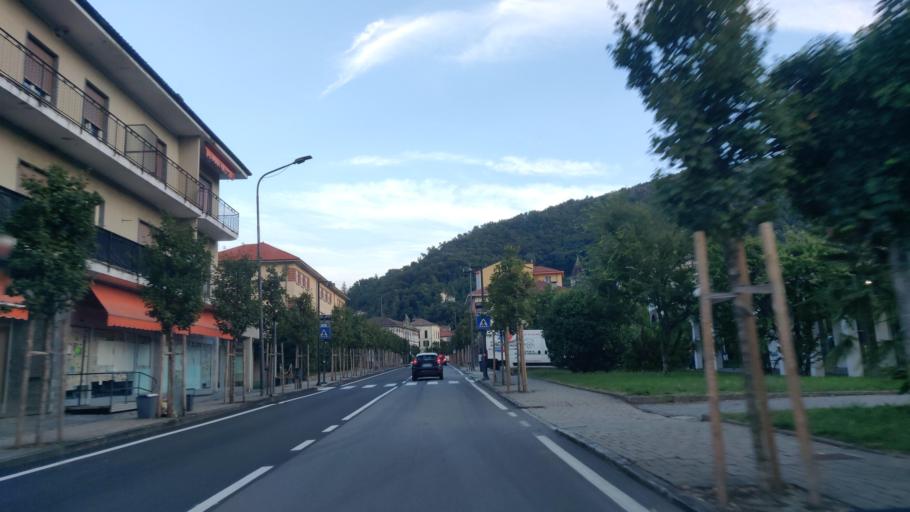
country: IT
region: Piedmont
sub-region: Provincia Verbano-Cusio-Ossola
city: Cannobio
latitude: 46.0642
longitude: 8.6968
